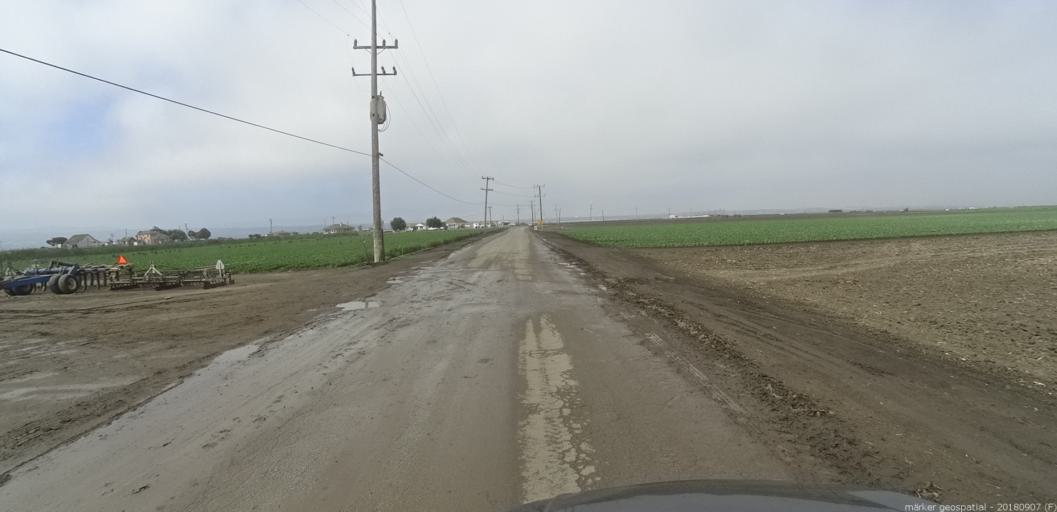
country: US
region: California
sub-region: Monterey County
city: Boronda
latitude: 36.6928
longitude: -121.7050
